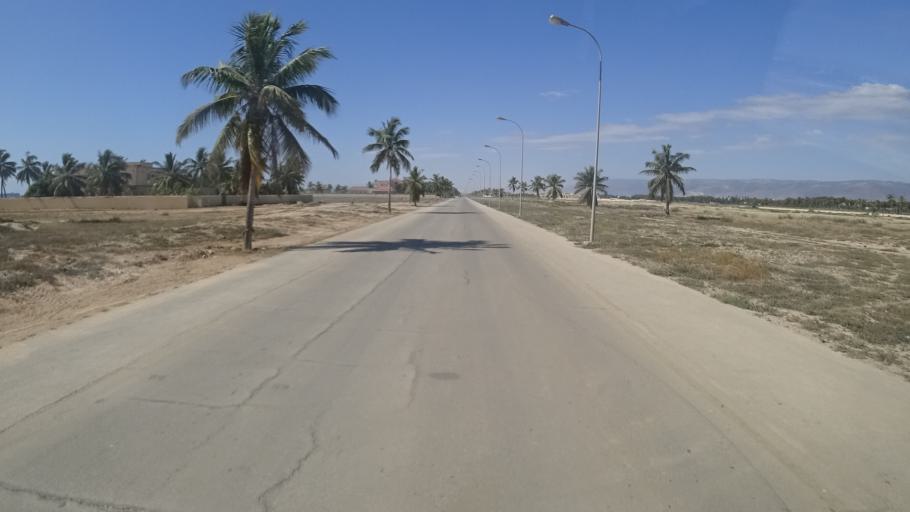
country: OM
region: Zufar
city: Salalah
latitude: 16.9955
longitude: 54.0605
